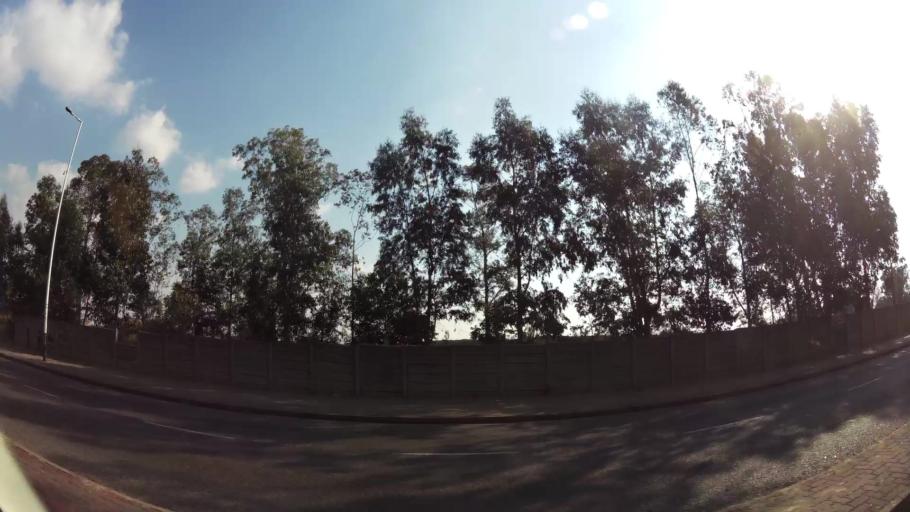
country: ZA
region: Gauteng
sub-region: Ekurhuleni Metropolitan Municipality
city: Boksburg
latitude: -26.2124
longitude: 28.2536
